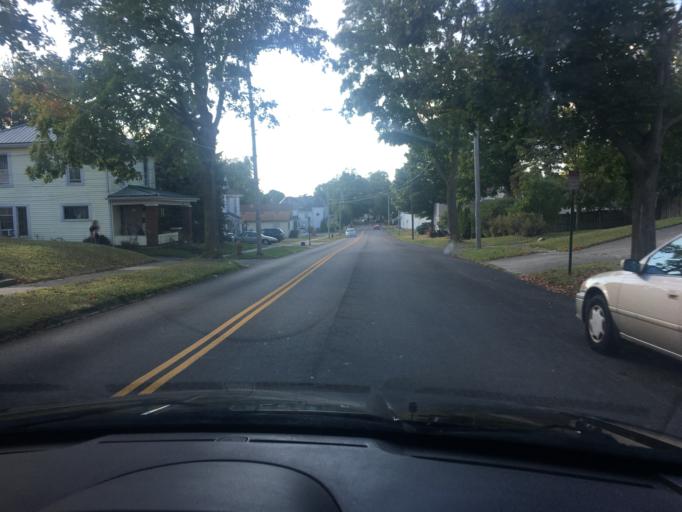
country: US
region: Ohio
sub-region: Logan County
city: Bellefontaine
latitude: 40.3586
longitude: -83.7506
